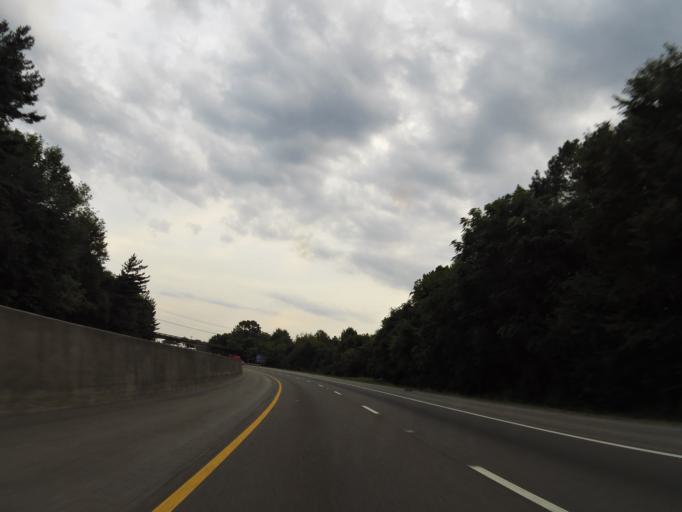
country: US
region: Tennessee
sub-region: Anderson County
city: Clinton
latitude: 36.0686
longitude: -84.0111
